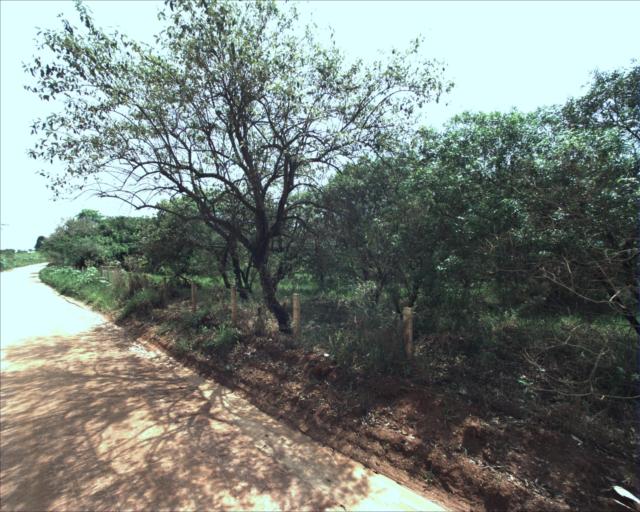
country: BR
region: Sao Paulo
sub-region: Aracoiaba Da Serra
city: Aracoiaba da Serra
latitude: -23.5577
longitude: -47.5543
